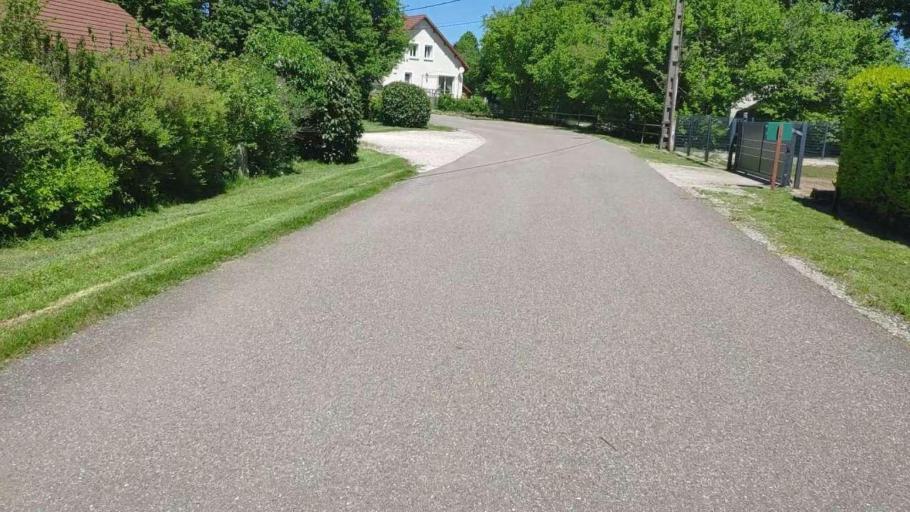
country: FR
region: Franche-Comte
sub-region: Departement du Jura
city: Poligny
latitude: 46.7332
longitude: 5.6916
